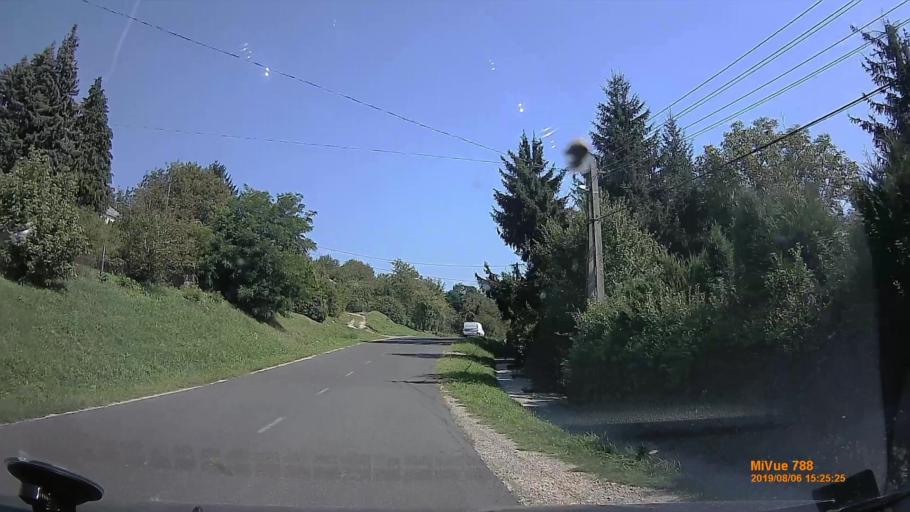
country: HR
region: Koprivnicko-Krizevacka
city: Drnje
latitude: 46.2546
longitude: 16.9455
